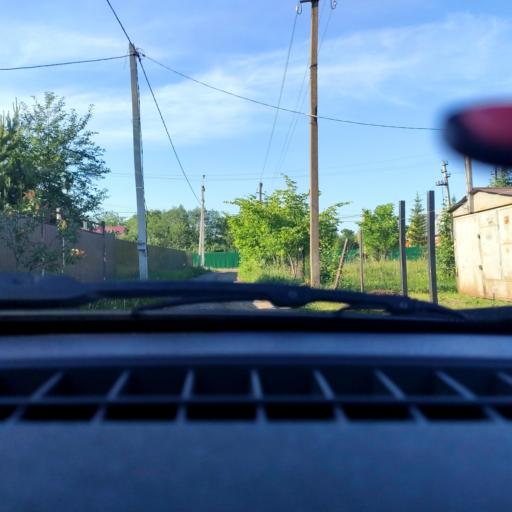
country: RU
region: Bashkortostan
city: Avdon
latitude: 54.4650
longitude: 55.8202
